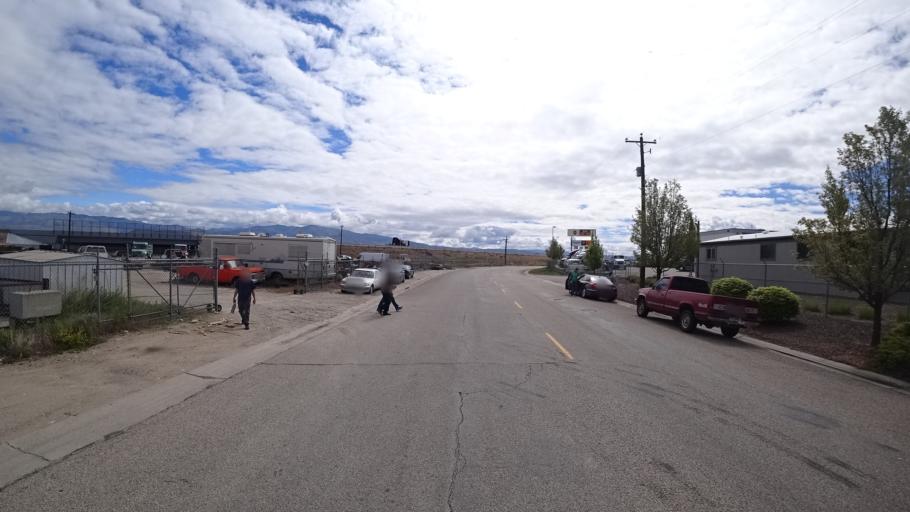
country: US
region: Idaho
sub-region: Ada County
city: Boise
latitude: 43.5628
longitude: -116.1919
